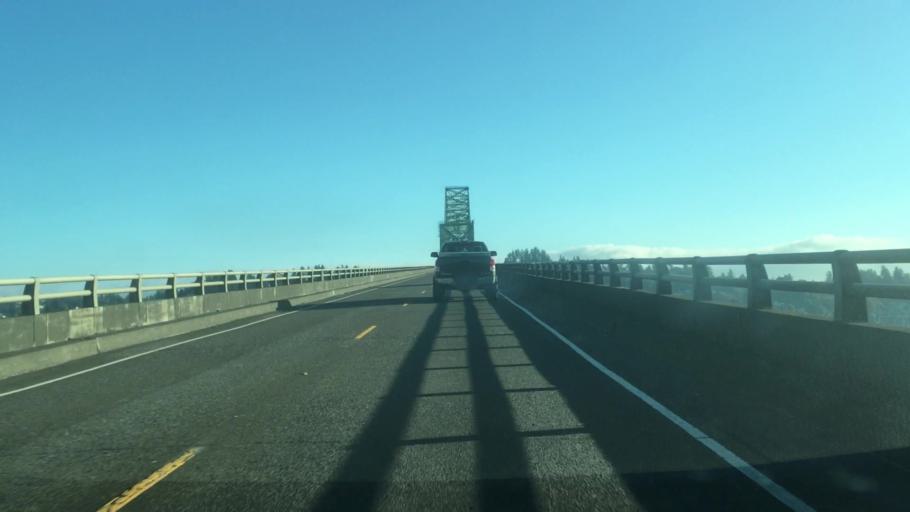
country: US
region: Oregon
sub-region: Clatsop County
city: Astoria
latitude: 46.1998
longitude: -123.8541
